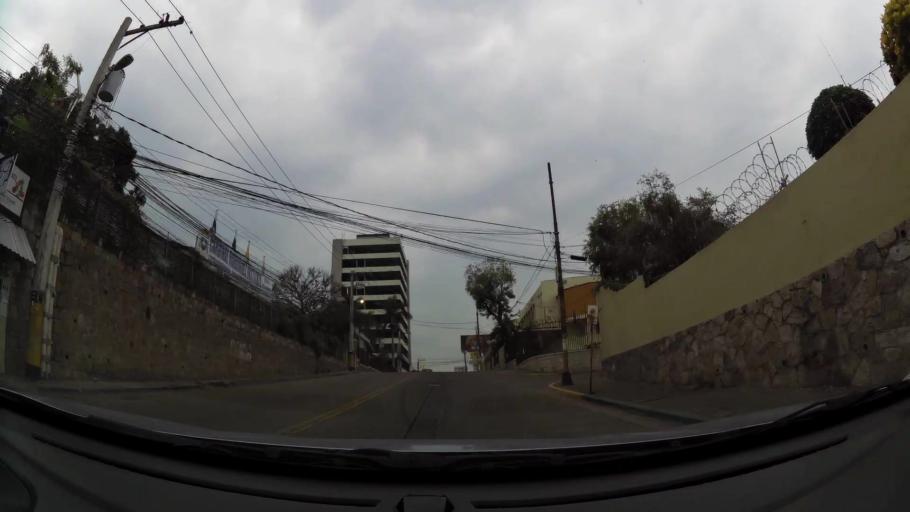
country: HN
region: Francisco Morazan
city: Tegucigalpa
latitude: 14.1021
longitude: -87.1914
